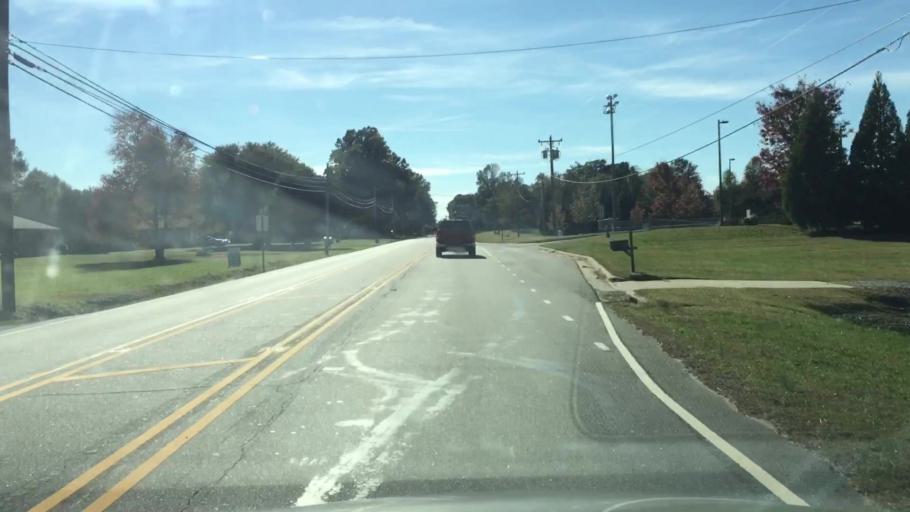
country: US
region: North Carolina
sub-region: Iredell County
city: Mooresville
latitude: 35.5959
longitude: -80.7831
